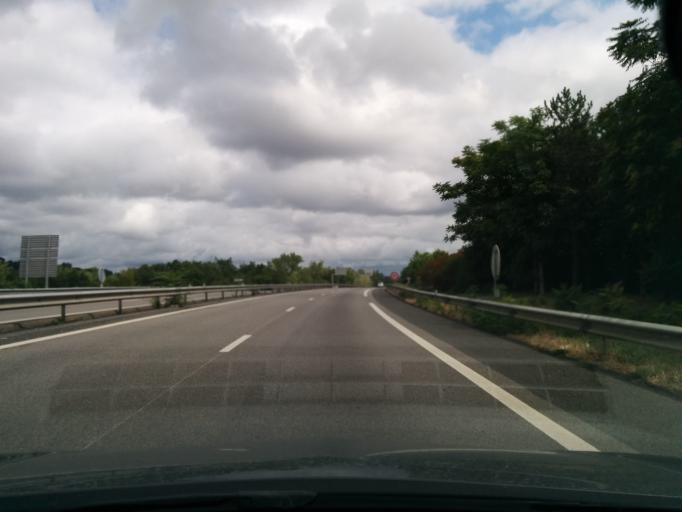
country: FR
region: Limousin
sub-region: Departement de la Correze
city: Varetz
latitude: 45.1654
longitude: 1.4800
